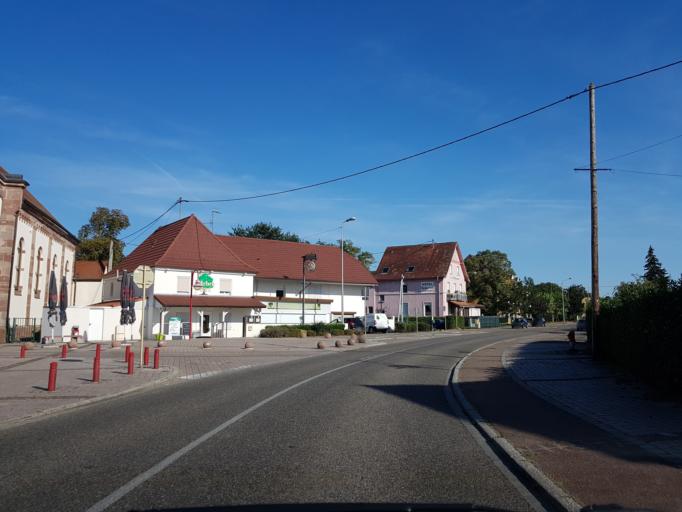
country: FR
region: Alsace
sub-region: Departement du Haut-Rhin
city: Pulversheim
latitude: 47.8381
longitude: 7.2982
